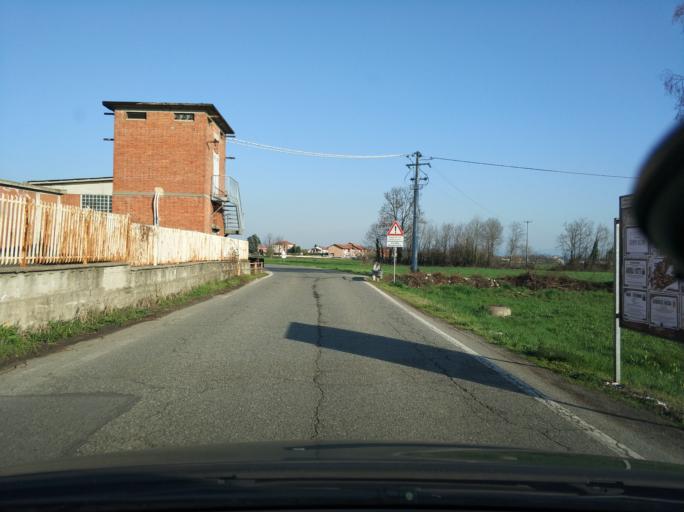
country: IT
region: Piedmont
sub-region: Provincia di Torino
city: San Maurizio
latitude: 45.1971
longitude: 7.6111
